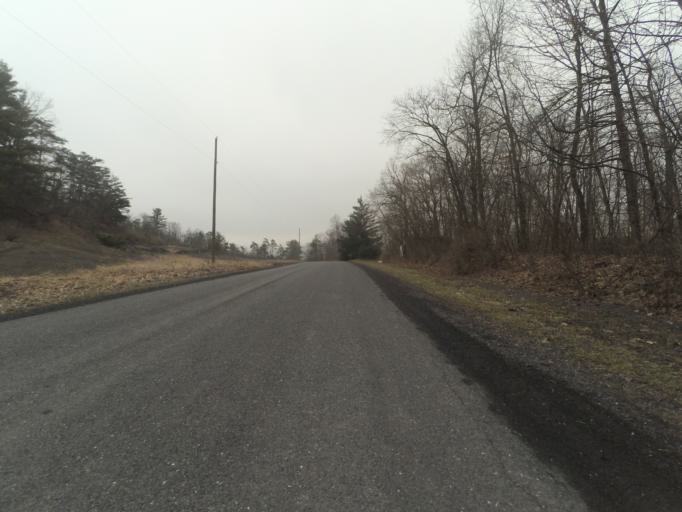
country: US
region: Pennsylvania
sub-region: Centre County
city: Centre Hall
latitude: 40.8710
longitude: -77.6210
